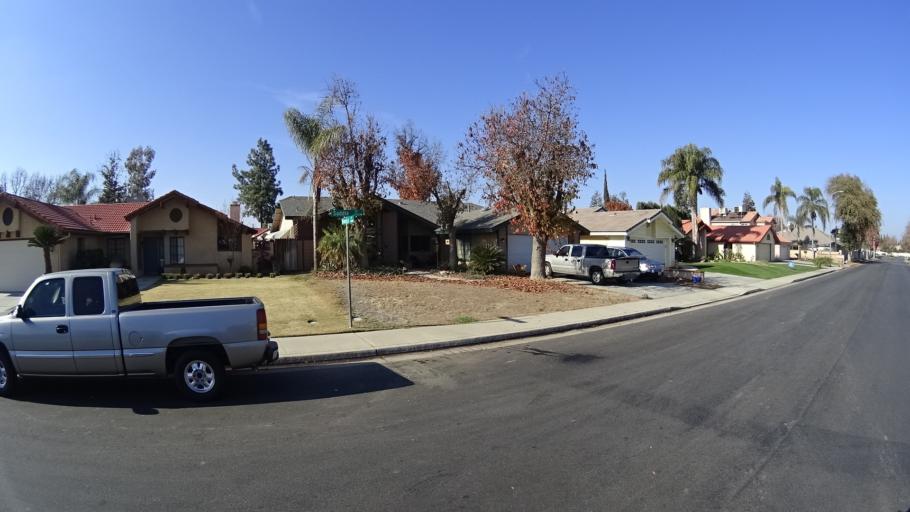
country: US
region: California
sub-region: Kern County
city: Greenacres
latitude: 35.3228
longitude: -119.1134
